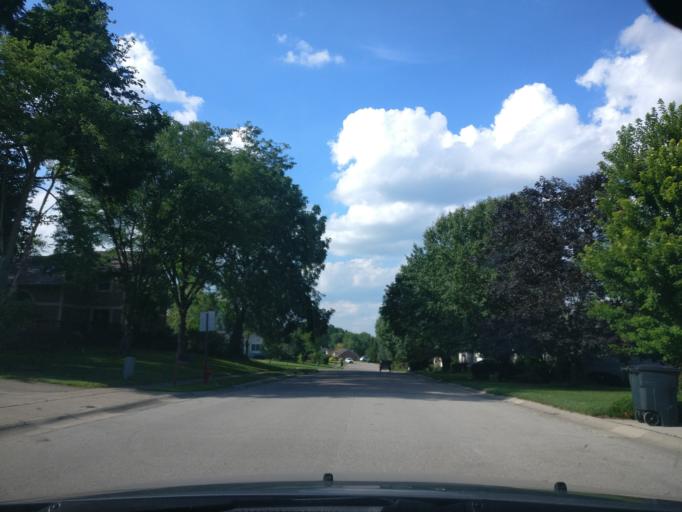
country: US
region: Ohio
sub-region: Warren County
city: Springboro
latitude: 39.5735
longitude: -84.2440
